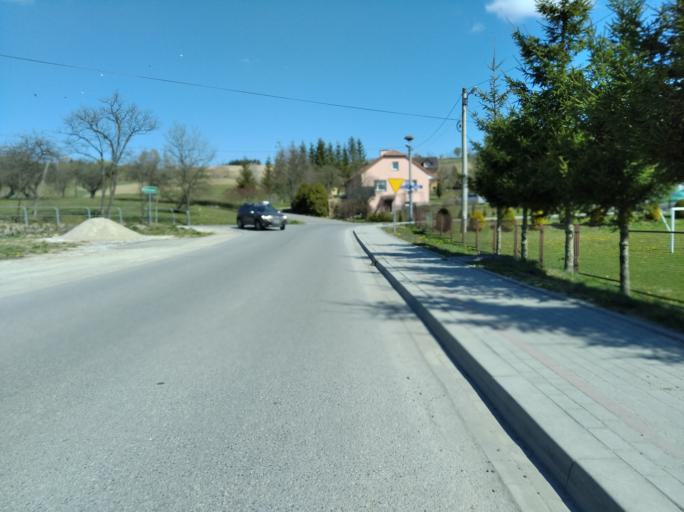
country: PL
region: Subcarpathian Voivodeship
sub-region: Powiat strzyzowski
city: Wisniowa
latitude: 49.9119
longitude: 21.6787
